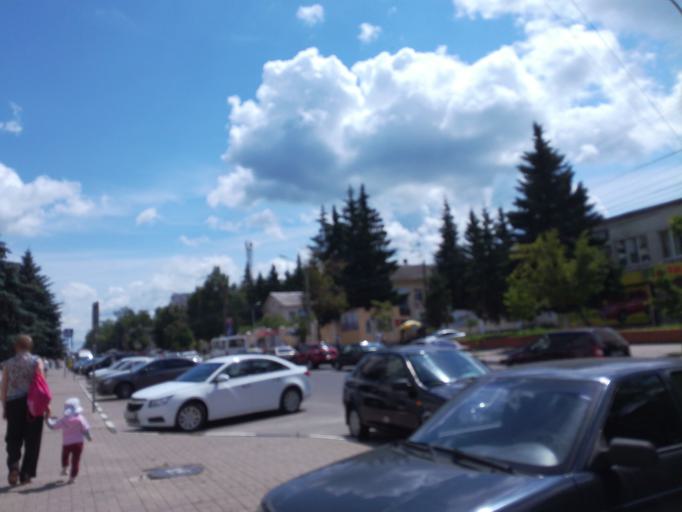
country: RU
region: Kursk
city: Kursk
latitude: 51.7470
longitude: 36.2439
